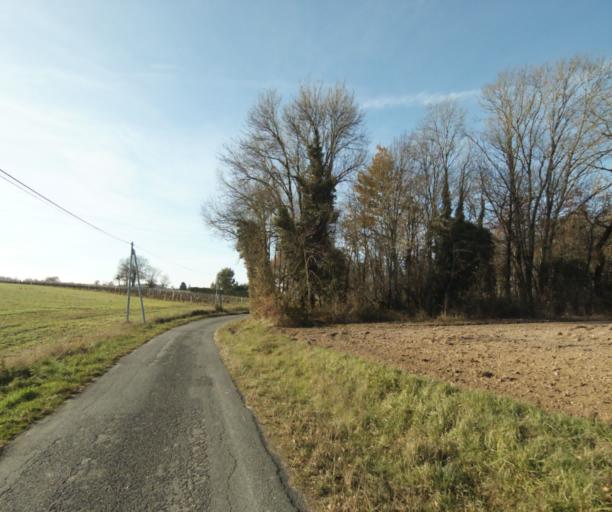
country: FR
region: Poitou-Charentes
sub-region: Departement de la Charente-Maritime
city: Cherac
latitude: 45.7455
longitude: -0.4878
